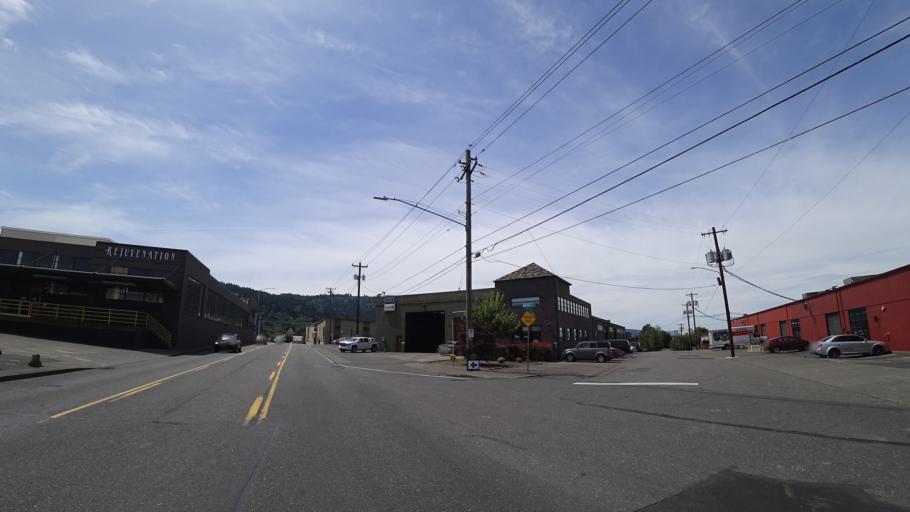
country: US
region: Oregon
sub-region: Multnomah County
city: Portland
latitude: 45.5403
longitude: -122.7039
